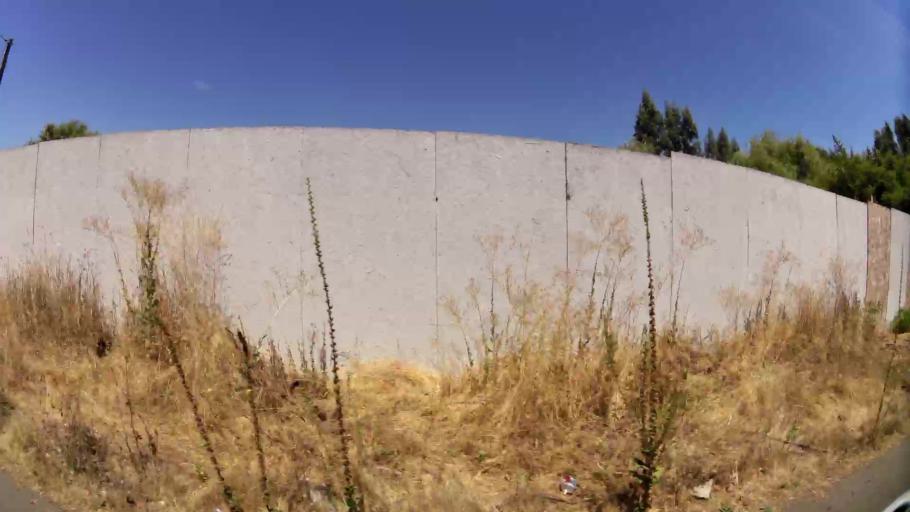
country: CL
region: Maule
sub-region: Provincia de Curico
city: Curico
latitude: -34.9975
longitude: -71.2123
